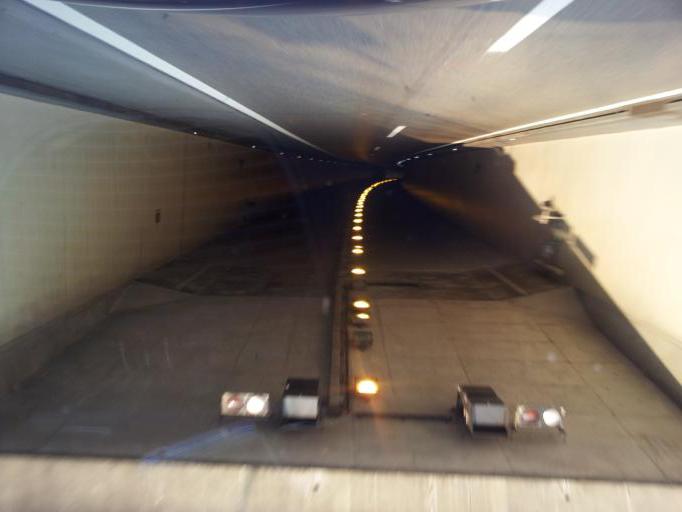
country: CH
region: Aargau
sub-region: Bezirk Brugg
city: Schinznach Dorf
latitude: 47.4559
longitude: 8.1439
